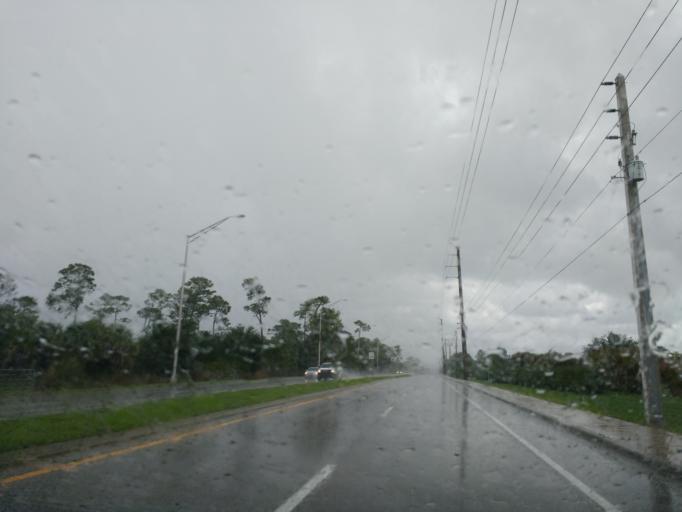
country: US
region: Florida
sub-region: Charlotte County
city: Charlotte Park
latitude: 26.8713
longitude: -82.0238
